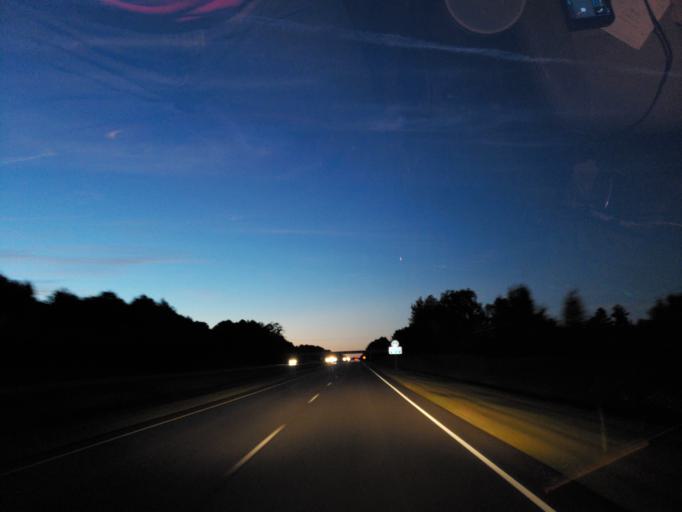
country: US
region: Mississippi
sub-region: Clarke County
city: Quitman
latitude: 32.0733
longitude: -88.6869
